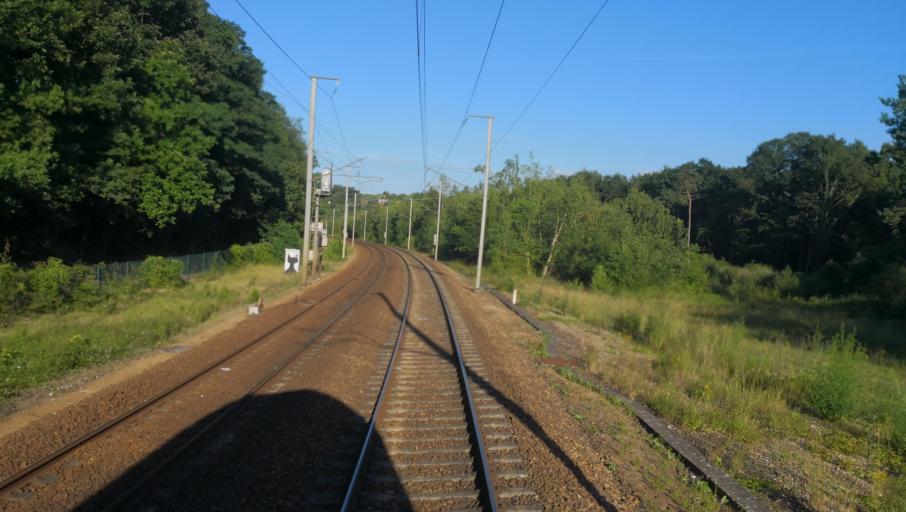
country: FR
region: Haute-Normandie
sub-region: Departement de l'Eure
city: Conches-en-Ouche
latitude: 48.9627
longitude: 0.9287
